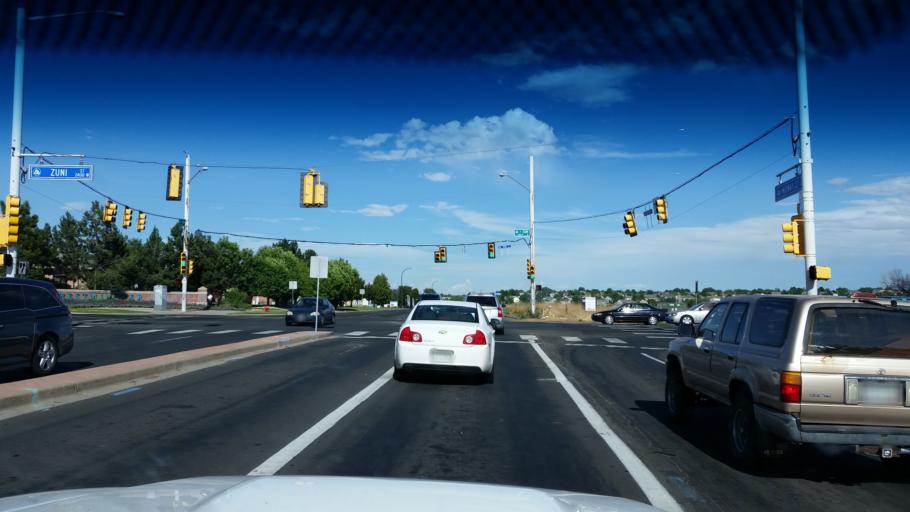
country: US
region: Colorado
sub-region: Adams County
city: Northglenn
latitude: 39.9284
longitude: -105.0160
